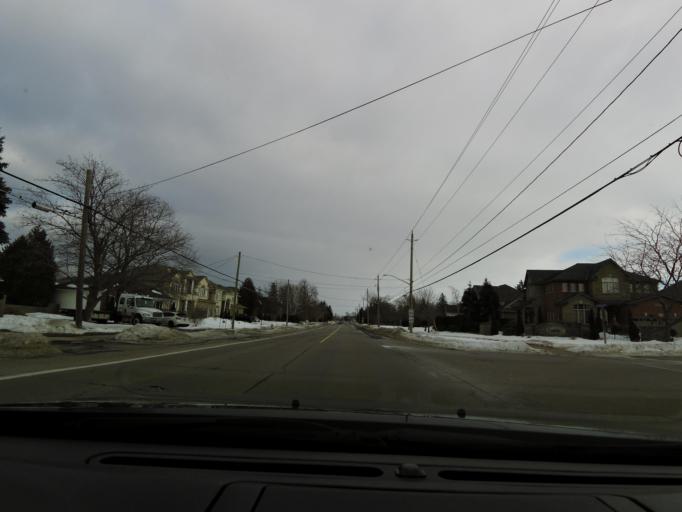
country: CA
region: Ontario
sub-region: Regional Municipality of Niagara
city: St. Catharines
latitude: 43.1854
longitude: -79.5330
